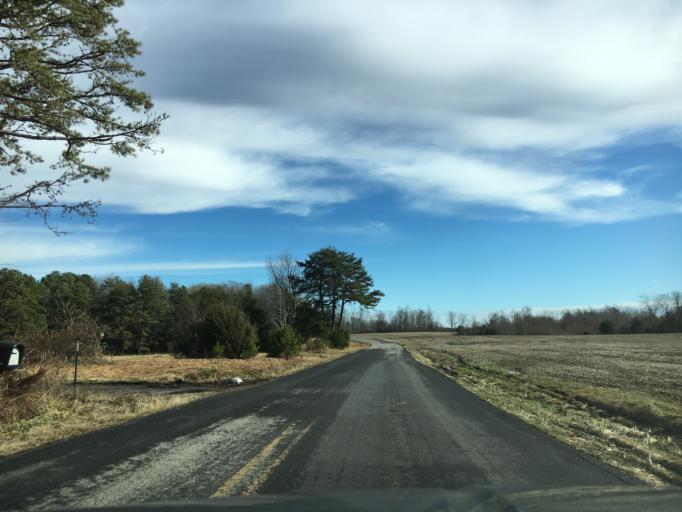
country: US
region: Virginia
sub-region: Nottoway County
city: Crewe
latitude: 37.3142
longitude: -78.1852
